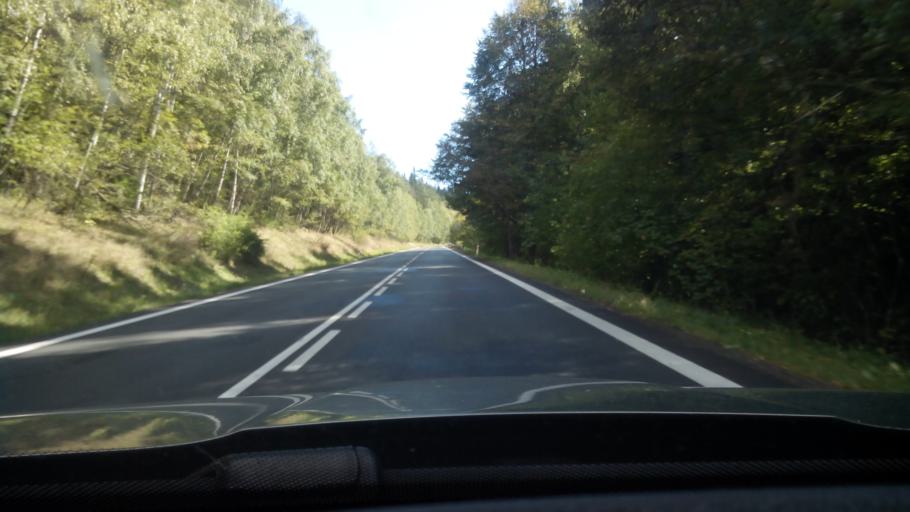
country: CZ
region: Jihocesky
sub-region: Okres Prachatice
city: Zdikov
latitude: 49.0745
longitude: 13.7078
